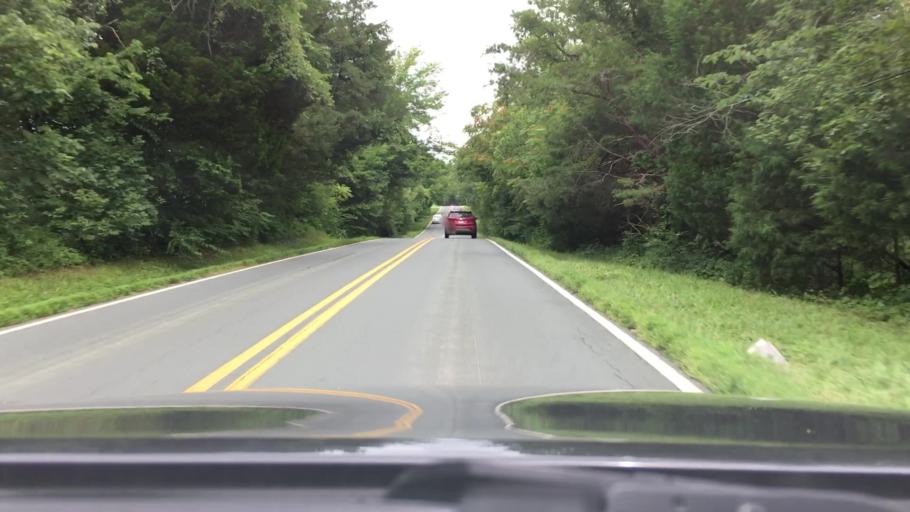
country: US
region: Virginia
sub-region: City of Charlottesville
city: Charlottesville
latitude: 38.0188
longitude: -78.3744
